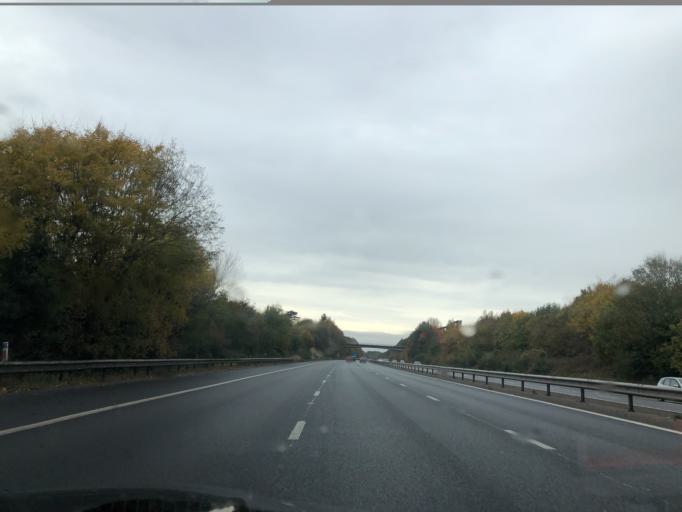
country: GB
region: England
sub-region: Hampshire
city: Old Basing
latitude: 51.2622
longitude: -1.0362
